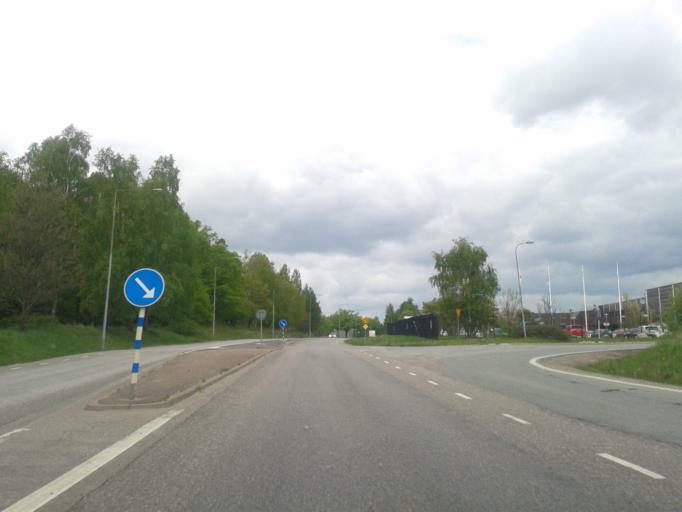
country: SE
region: Vaestra Goetaland
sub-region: Goteborg
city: Eriksbo
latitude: 57.7816
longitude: 12.0483
